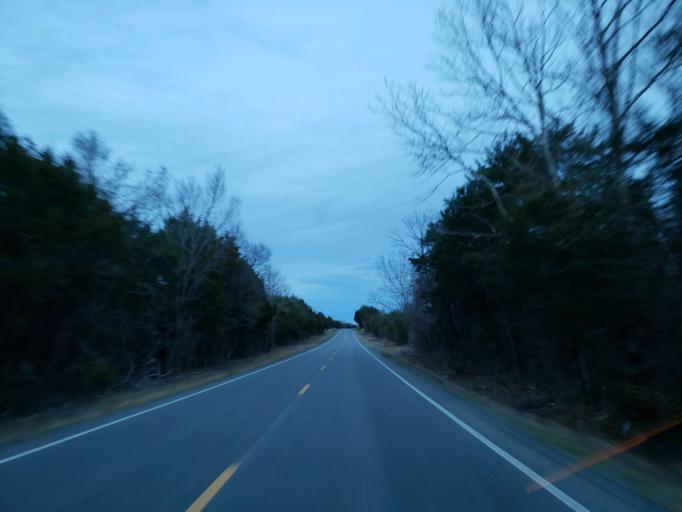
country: US
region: Alabama
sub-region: Sumter County
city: Livingston
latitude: 32.8097
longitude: -88.2210
